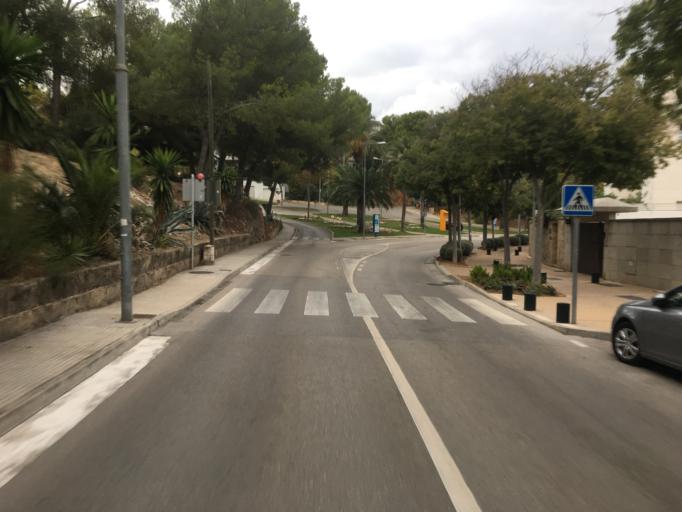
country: ES
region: Balearic Islands
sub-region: Illes Balears
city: Palma
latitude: 39.5462
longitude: 2.5953
